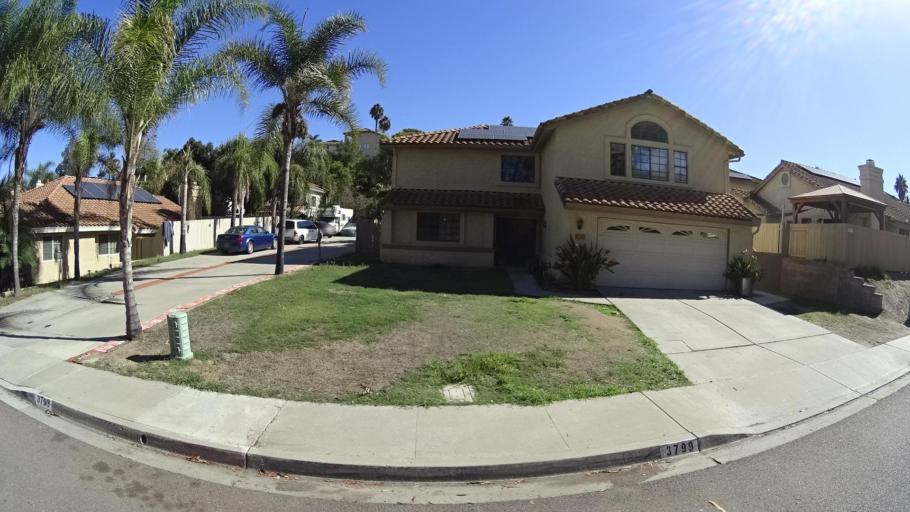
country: US
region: California
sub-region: San Diego County
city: Bonita
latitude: 32.6663
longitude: -117.0160
